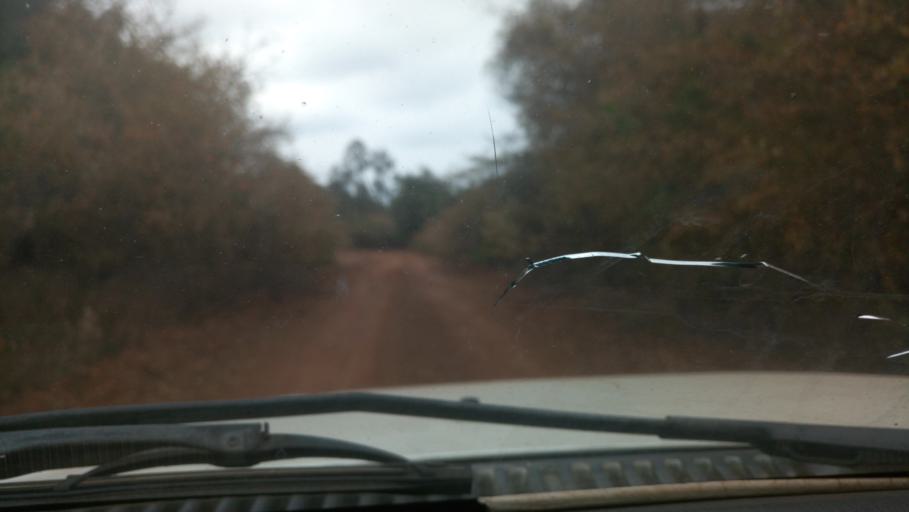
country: KE
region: Nairobi Area
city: Nairobi
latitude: -1.3766
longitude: 36.7703
